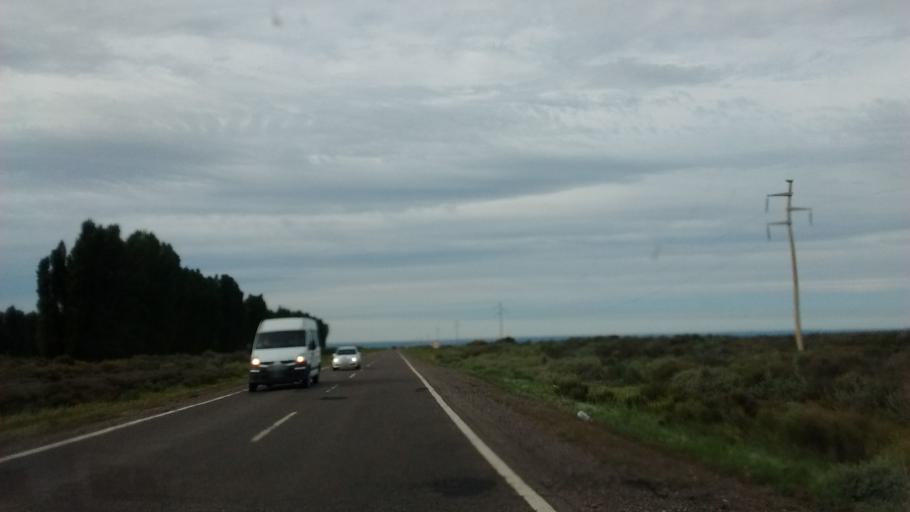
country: AR
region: Rio Negro
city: Catriel
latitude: -37.9362
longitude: -67.8824
